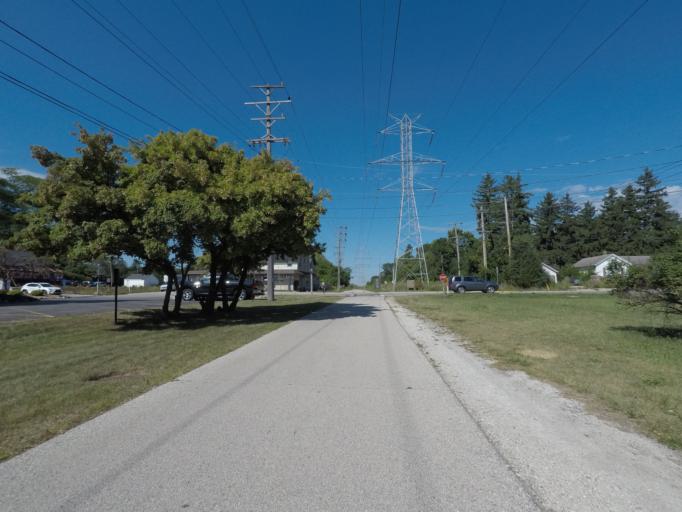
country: US
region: Wisconsin
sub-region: Waukesha County
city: New Berlin
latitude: 43.0104
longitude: -88.1268
